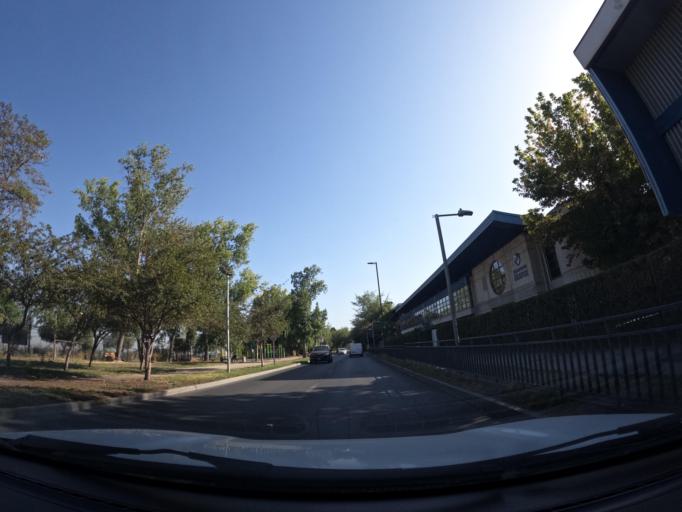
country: CL
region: Santiago Metropolitan
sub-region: Provincia de Santiago
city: Villa Presidente Frei, Nunoa, Santiago, Chile
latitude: -33.4911
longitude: -70.5584
